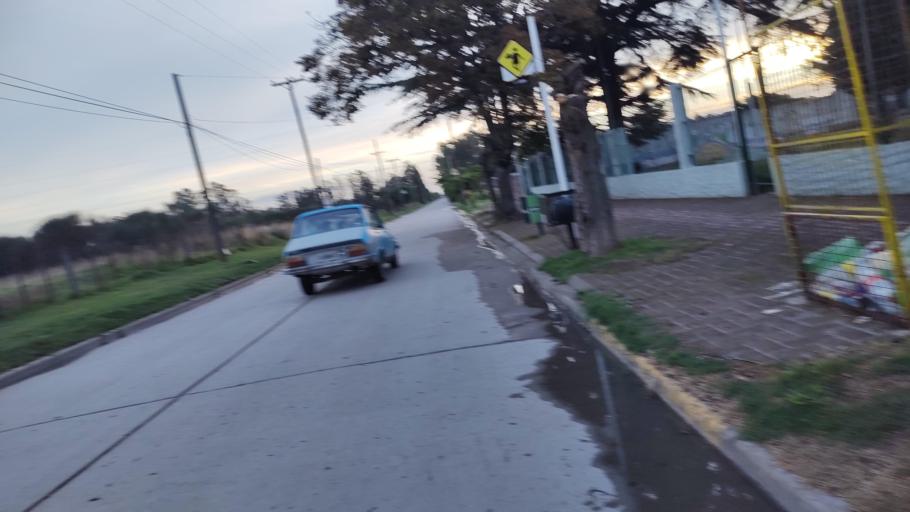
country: AR
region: Buenos Aires
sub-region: Partido de Loberia
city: Loberia
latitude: -38.1769
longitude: -58.7775
